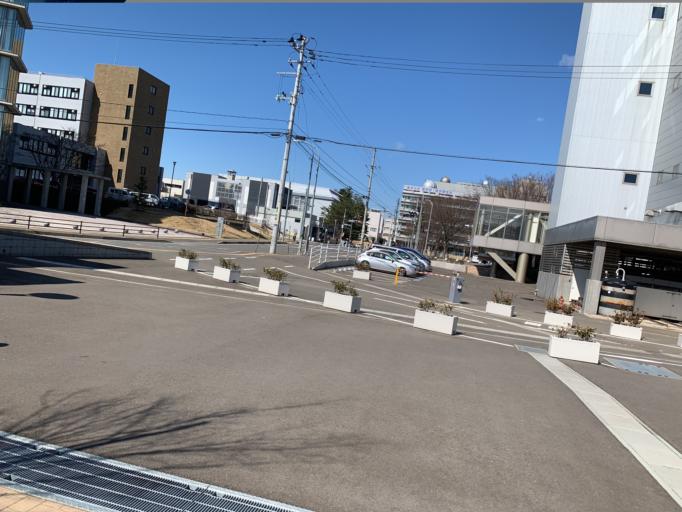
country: JP
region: Miyagi
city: Sendai
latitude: 38.2554
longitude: 140.8357
